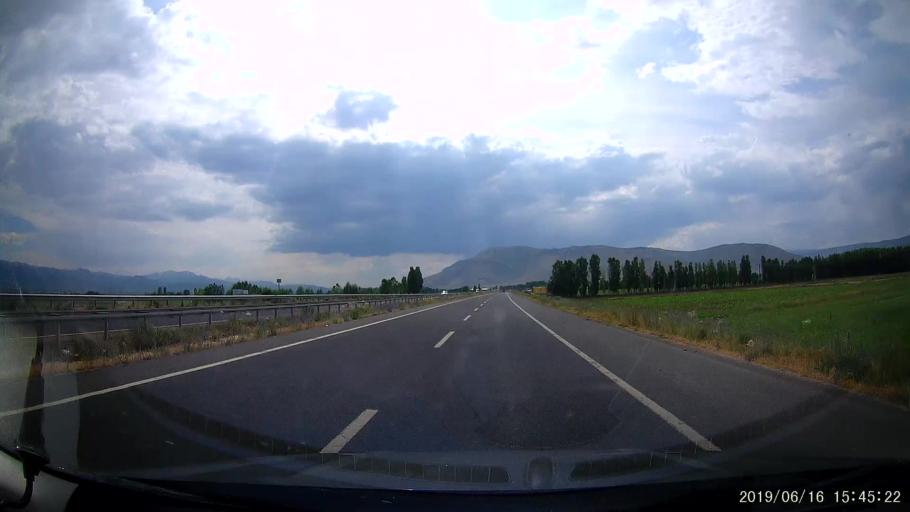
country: TR
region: Erzurum
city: Pasinler
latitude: 39.9883
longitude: 41.7678
